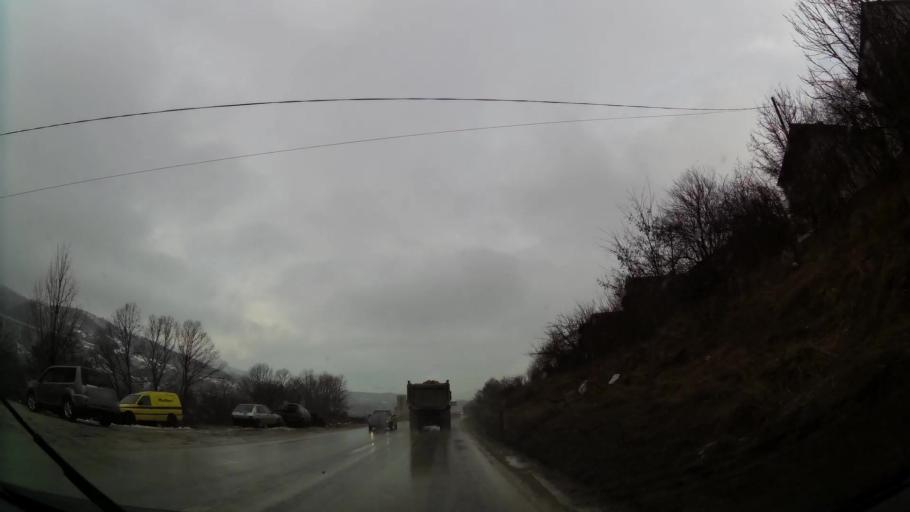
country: XK
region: Ferizaj
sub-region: Komuna e Kacanikut
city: Kacanik
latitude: 42.2338
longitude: 21.2509
